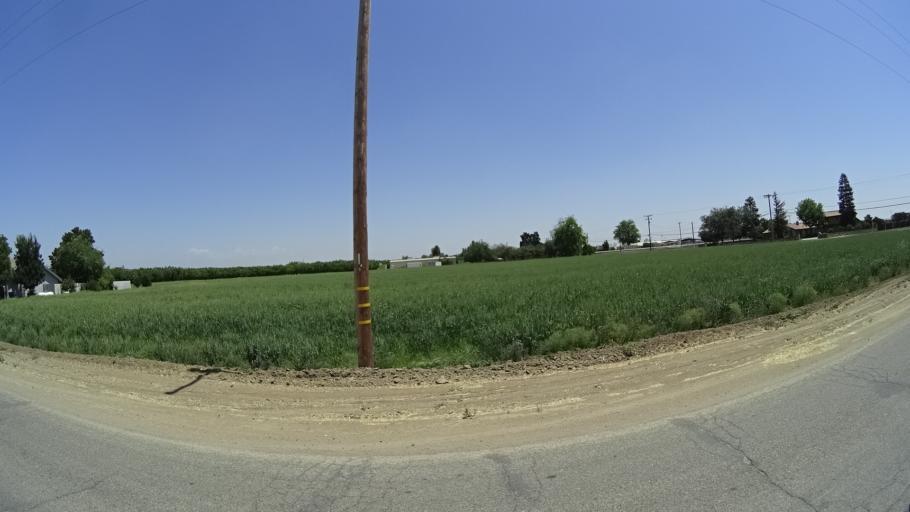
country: US
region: California
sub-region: Kings County
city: Armona
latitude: 36.3433
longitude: -119.7269
